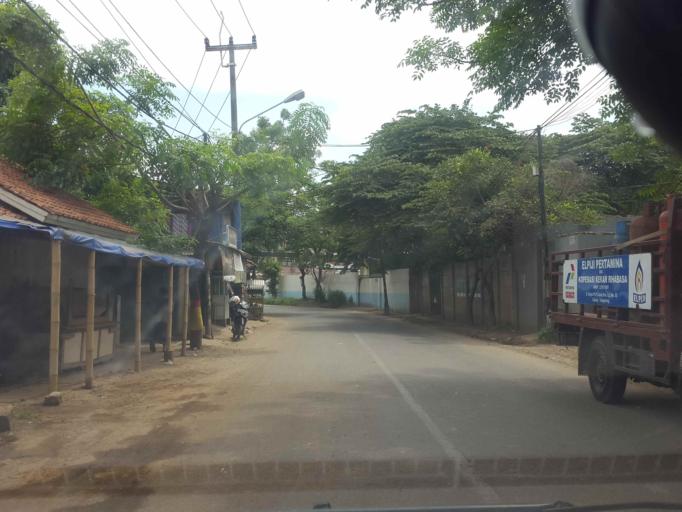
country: ID
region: Banten
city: Tangerang
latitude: -6.1507
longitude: 106.6215
